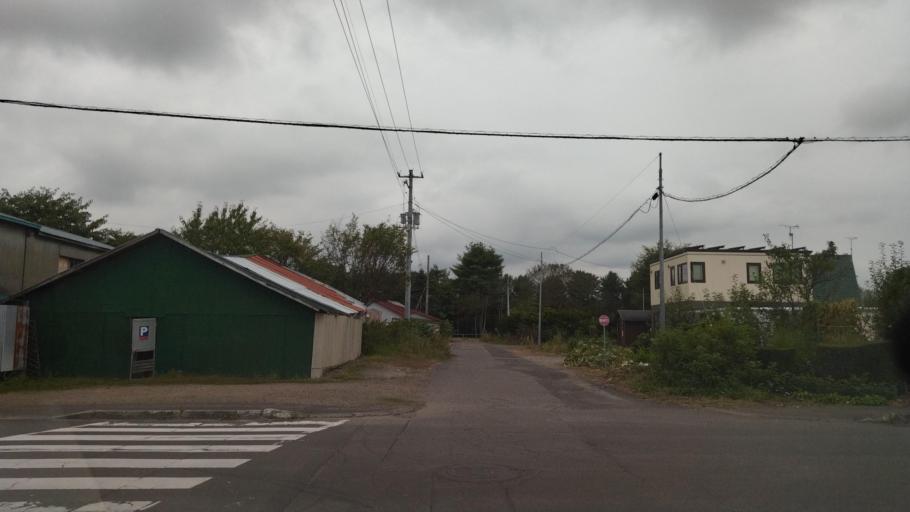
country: JP
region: Hokkaido
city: Otofuke
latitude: 43.2303
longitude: 143.2905
